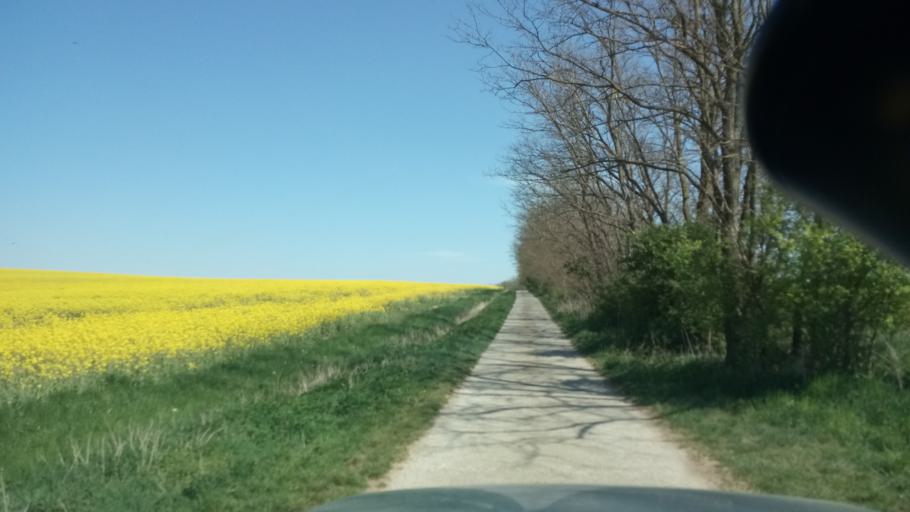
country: HU
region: Zala
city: Pacsa
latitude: 46.7044
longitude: 17.0882
